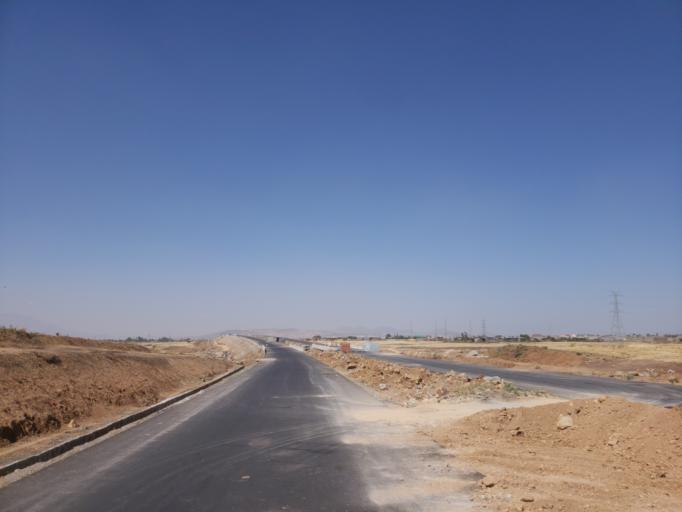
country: ET
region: Oromiya
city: Mojo
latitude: 8.5682
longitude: 39.1479
